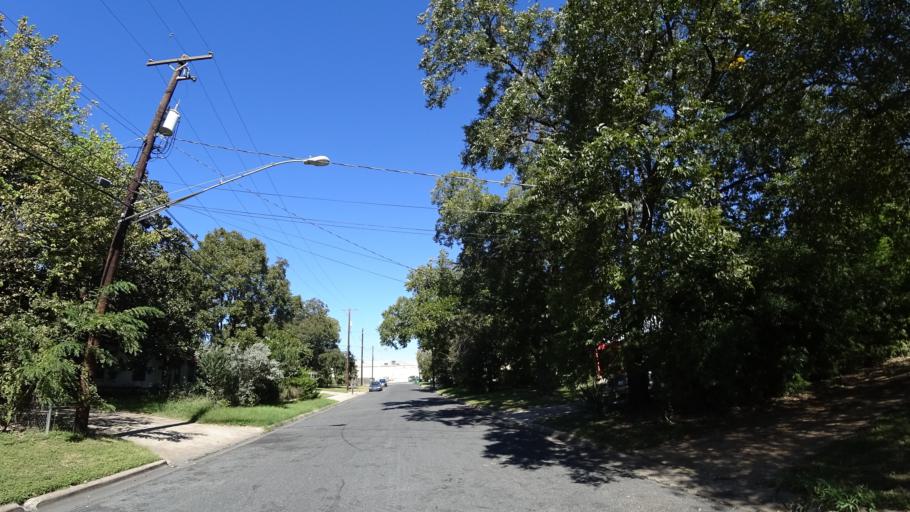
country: US
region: Texas
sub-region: Travis County
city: Rollingwood
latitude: 30.2255
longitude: -97.7854
